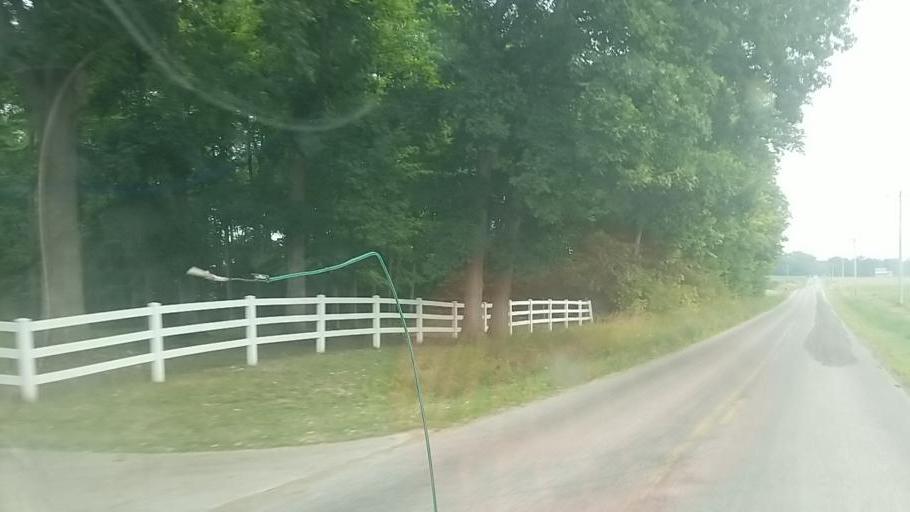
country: US
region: Ohio
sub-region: Ashland County
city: Ashland
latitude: 40.9184
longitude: -82.3876
